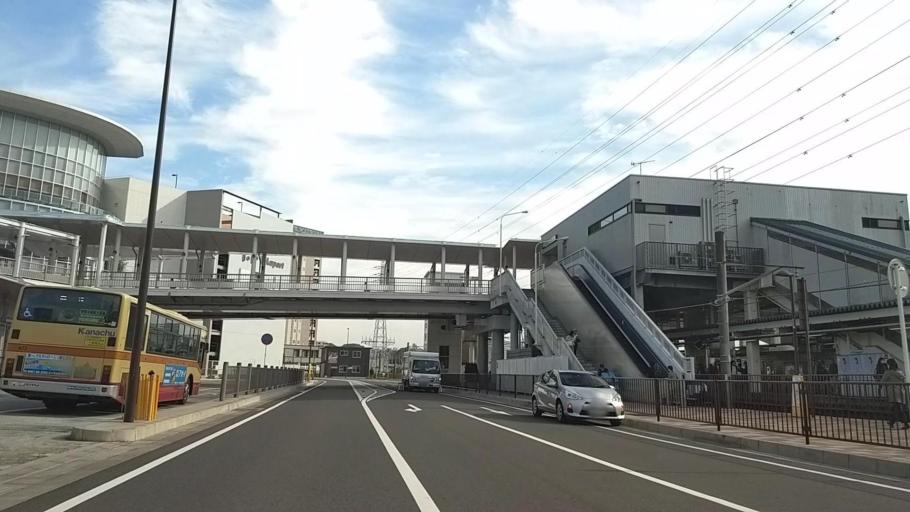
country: JP
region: Kanagawa
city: Atsugi
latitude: 35.4541
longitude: 139.3884
